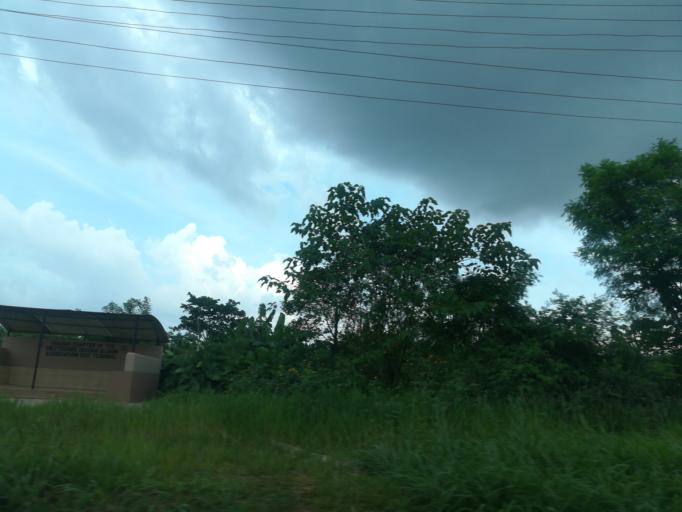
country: NG
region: Oyo
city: Ibadan
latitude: 7.4382
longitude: 3.8837
